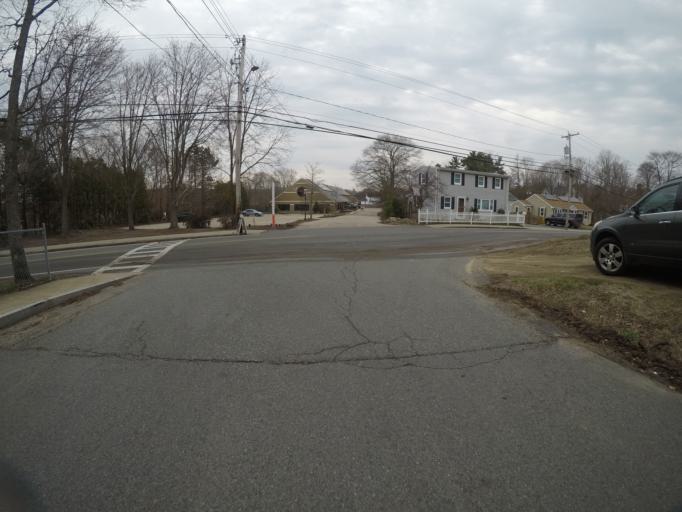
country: US
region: Massachusetts
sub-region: Bristol County
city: Easton
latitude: 42.0716
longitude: -71.1040
